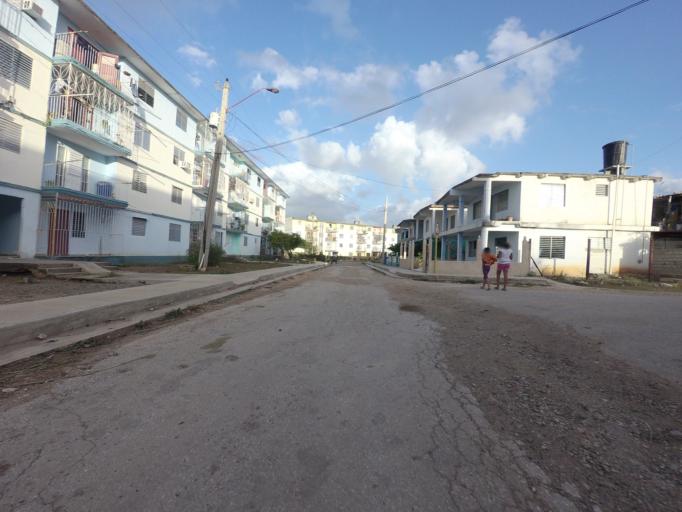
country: CU
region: Ciego de Avila
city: Ciego de Avila
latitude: 21.8440
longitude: -78.7488
